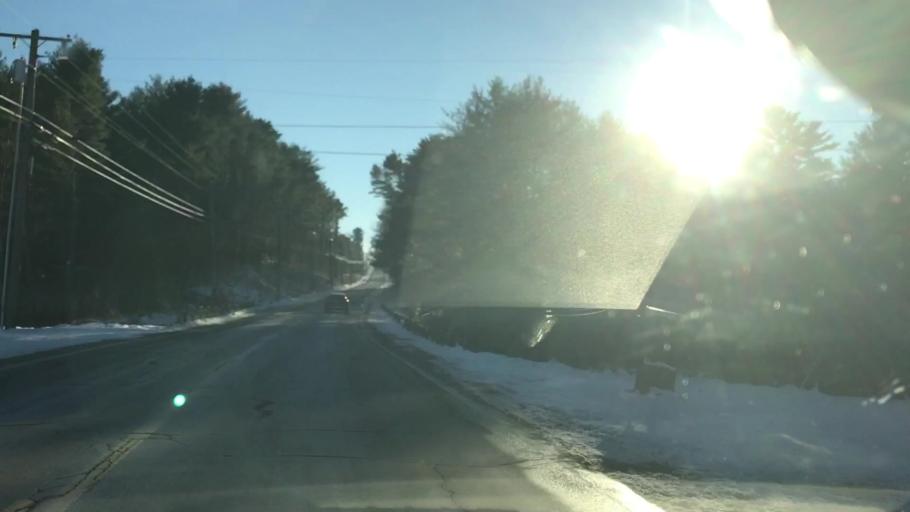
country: US
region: New Hampshire
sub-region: Grafton County
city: Haverhill
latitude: 44.0572
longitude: -72.0502
